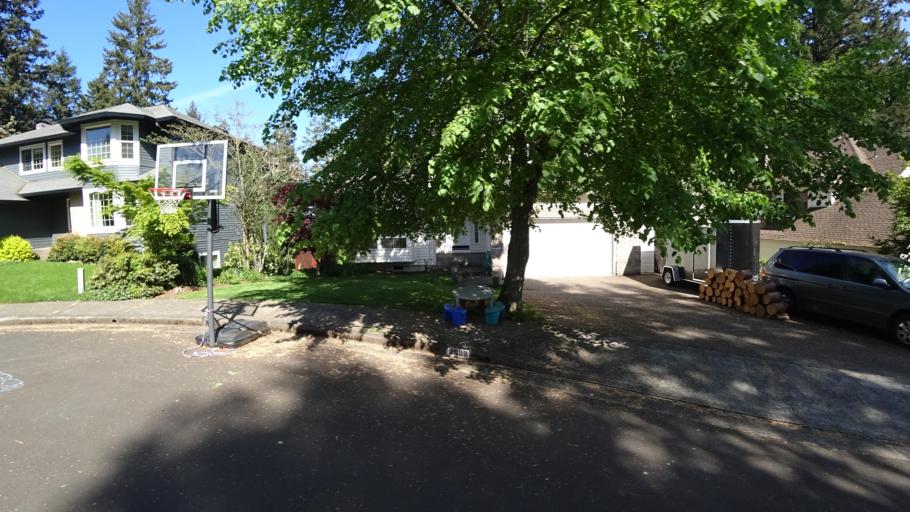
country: US
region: Oregon
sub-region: Washington County
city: Aloha
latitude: 45.4715
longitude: -122.8399
